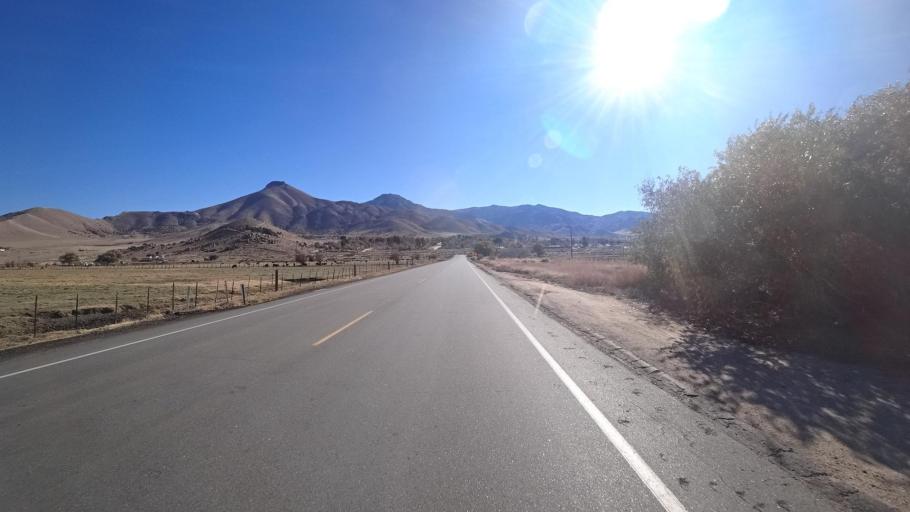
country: US
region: California
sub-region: Kern County
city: Weldon
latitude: 35.6595
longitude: -118.3229
